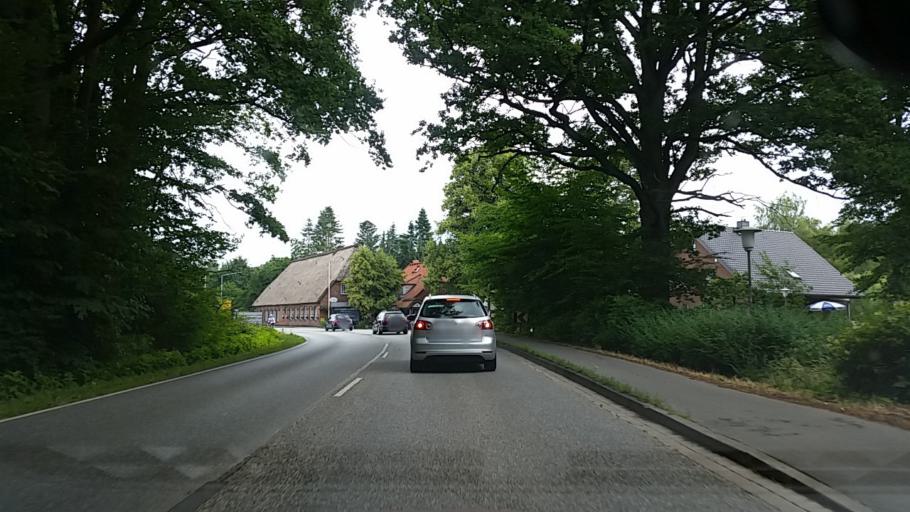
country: DE
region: Schleswig-Holstein
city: Kayhude
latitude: 53.7482
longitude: 10.1255
